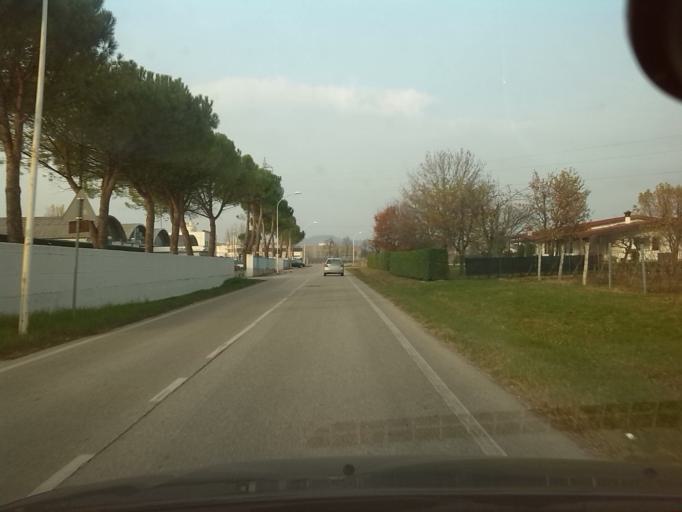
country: IT
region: Friuli Venezia Giulia
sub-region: Provincia di Udine
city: San Giovanni al Natisone
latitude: 45.9752
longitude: 13.4251
